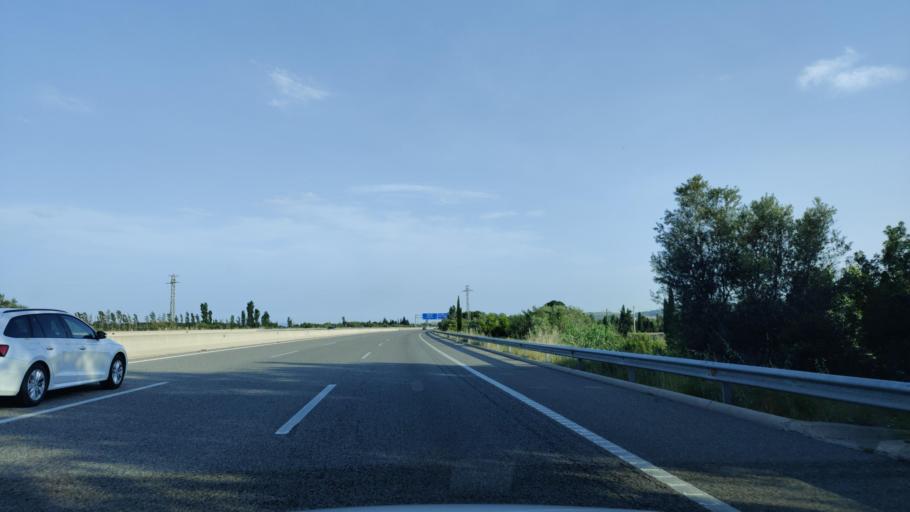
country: ES
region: Catalonia
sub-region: Provincia de Girona
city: Pont de Molins
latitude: 42.3143
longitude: 2.9447
